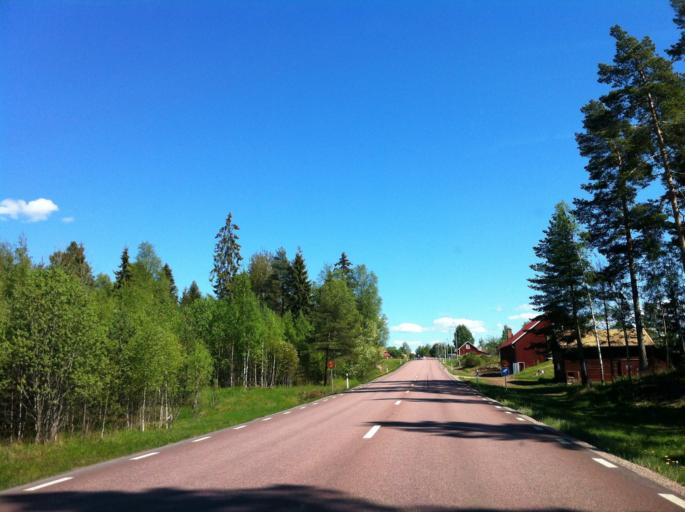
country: SE
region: Dalarna
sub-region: Leksand Municipality
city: Siljansnas
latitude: 60.9329
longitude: 14.7779
